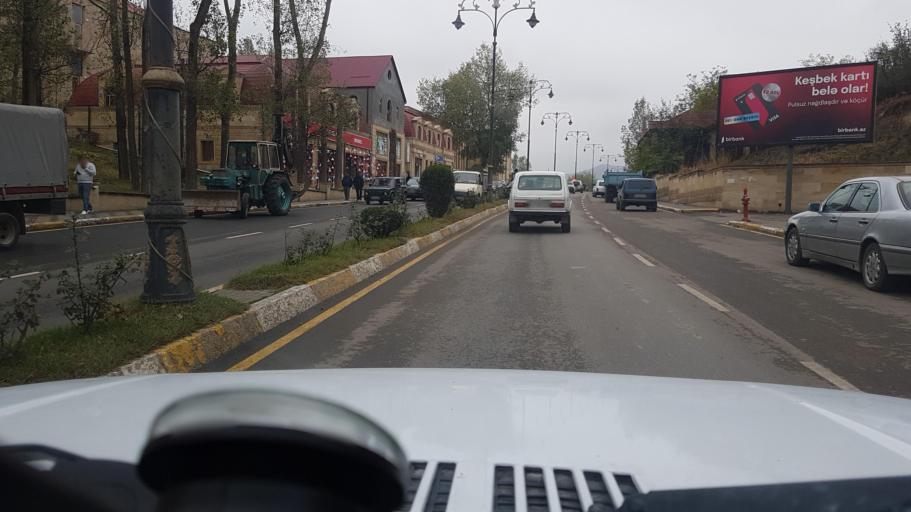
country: AZ
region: Gadabay Rayon
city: Kyadabek
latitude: 40.5773
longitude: 45.8087
